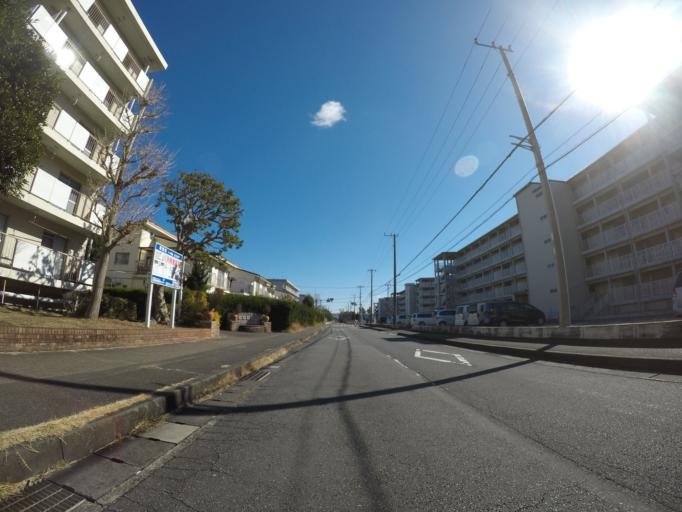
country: JP
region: Shizuoka
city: Numazu
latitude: 35.1288
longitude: 138.8070
